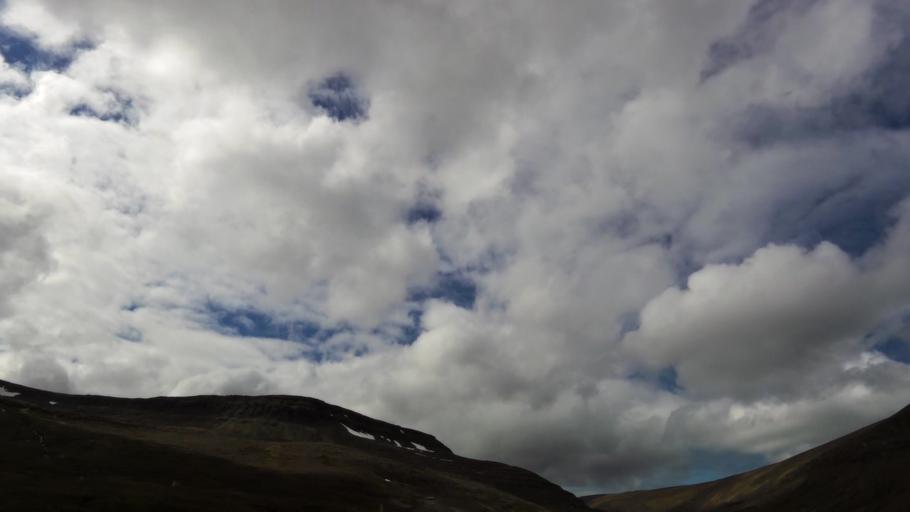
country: IS
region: Westfjords
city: Isafjoerdur
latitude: 66.1639
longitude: -23.3245
